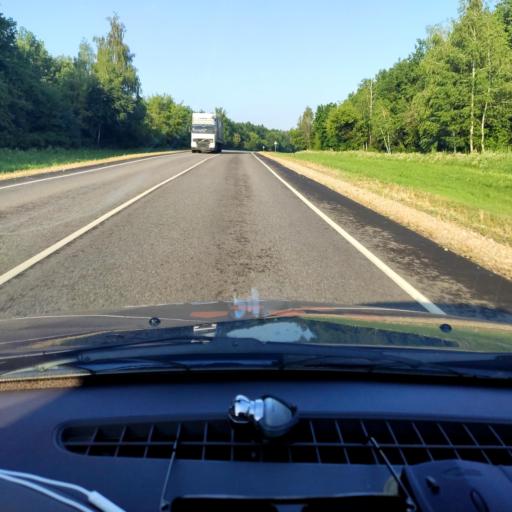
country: RU
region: Lipetsk
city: Izmalkovo
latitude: 52.4516
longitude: 37.9974
